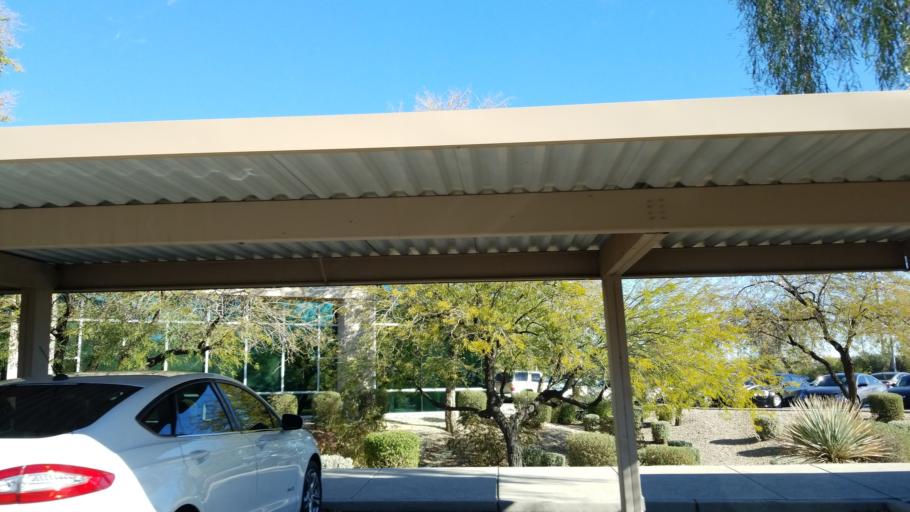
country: US
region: Arizona
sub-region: Maricopa County
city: Glendale
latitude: 33.6365
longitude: -112.1170
